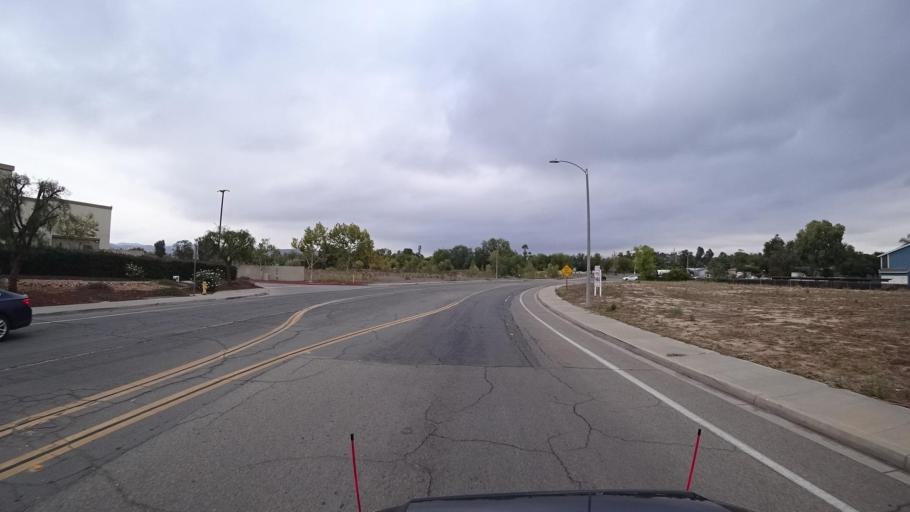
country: US
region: California
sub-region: San Diego County
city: Ramona
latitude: 33.0344
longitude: -116.8798
